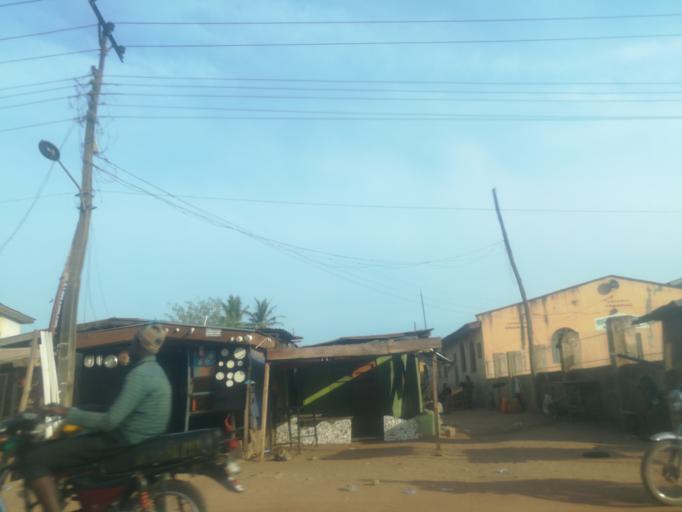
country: NG
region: Ogun
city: Abeokuta
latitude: 7.1202
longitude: 3.3199
